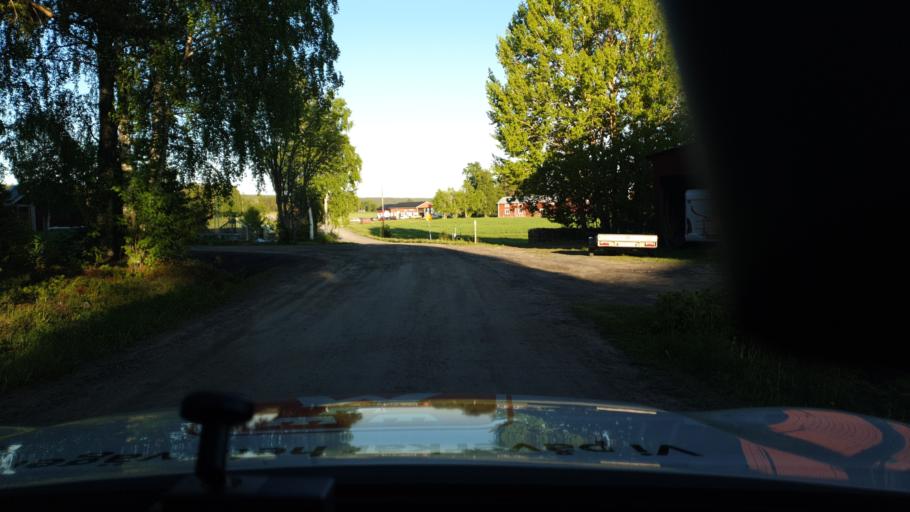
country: SE
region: Vaesterbotten
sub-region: Umea Kommun
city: Roback
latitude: 64.0066
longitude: 20.0683
